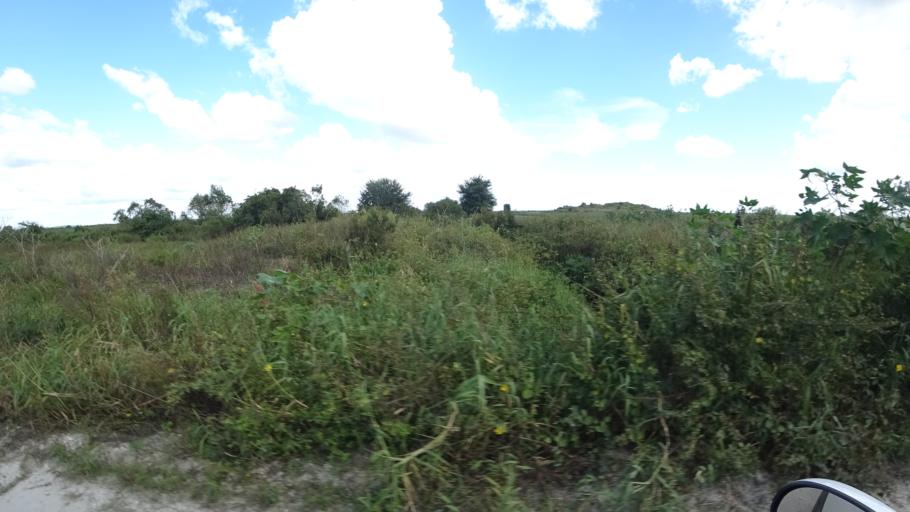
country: US
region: Florida
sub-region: DeSoto County
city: Arcadia
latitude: 27.3330
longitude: -82.1050
